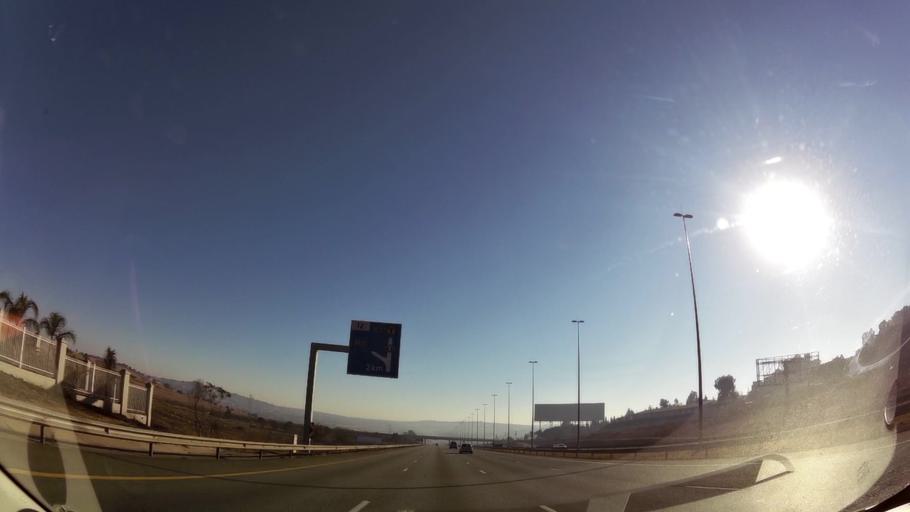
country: ZA
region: Gauteng
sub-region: City of Tshwane Metropolitan Municipality
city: Centurion
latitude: -25.8913
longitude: 28.2547
